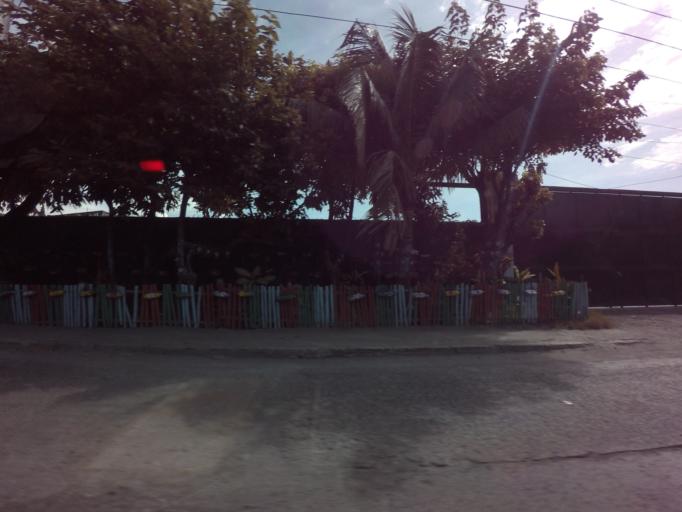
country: PH
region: Calabarzon
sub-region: Province of Rizal
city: Pateros
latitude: 14.5494
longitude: 121.0834
